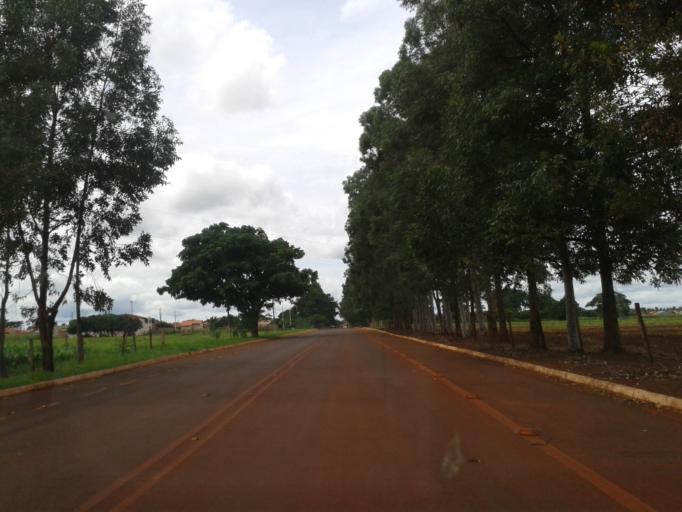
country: BR
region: Minas Gerais
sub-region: Centralina
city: Centralina
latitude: -18.5901
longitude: -49.2070
